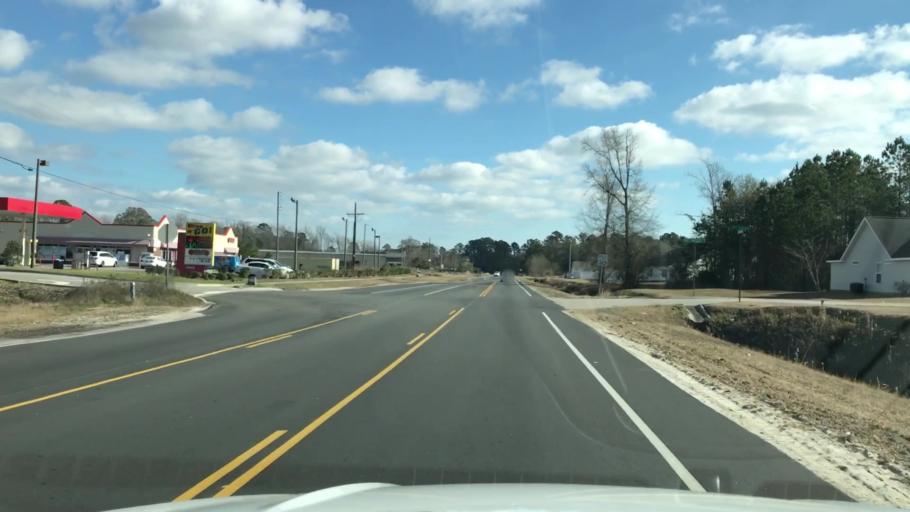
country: US
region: South Carolina
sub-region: Horry County
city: Socastee
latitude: 33.6772
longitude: -78.9762
